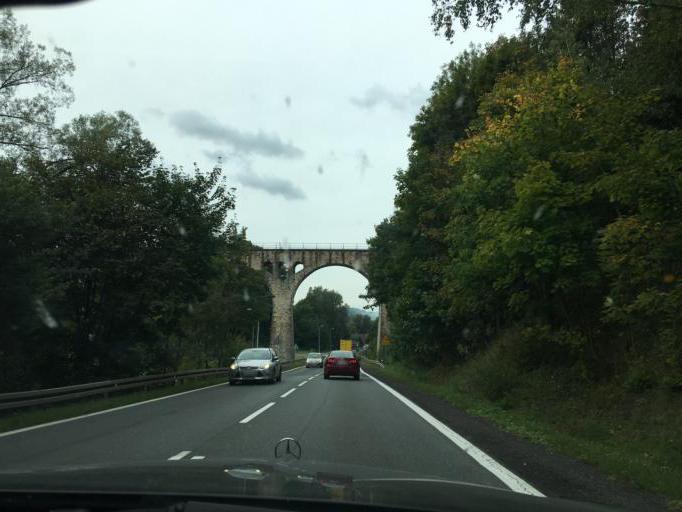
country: PL
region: Lower Silesian Voivodeship
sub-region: Powiat klodzki
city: Lewin Klodzki
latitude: 50.4069
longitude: 16.2834
